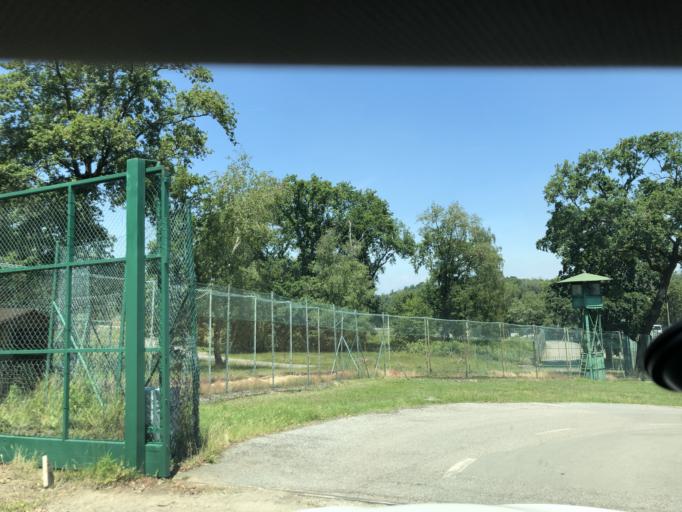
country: IT
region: Piedmont
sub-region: Provincia di Novara
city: Mezzomerico
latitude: 45.6379
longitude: 8.6122
